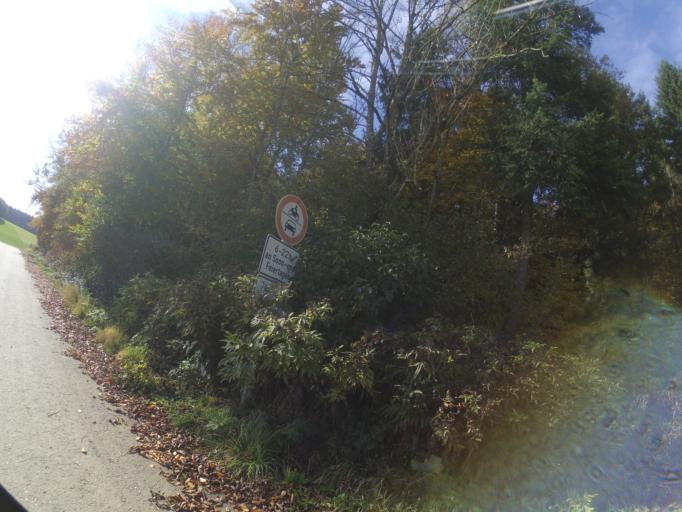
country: DE
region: Baden-Wuerttemberg
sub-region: Tuebingen Region
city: Weidenstetten
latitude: 48.5840
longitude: 9.9836
